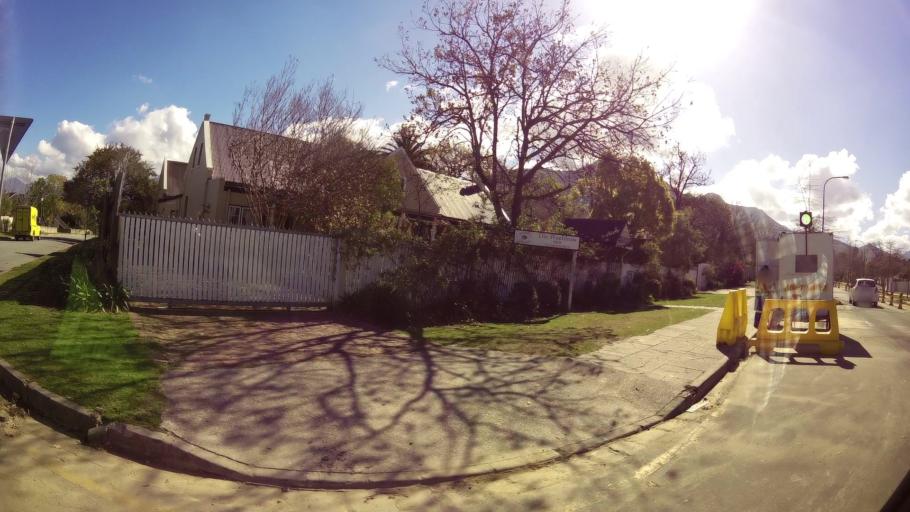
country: ZA
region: Western Cape
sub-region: Eden District Municipality
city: George
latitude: -33.9534
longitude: 22.4598
